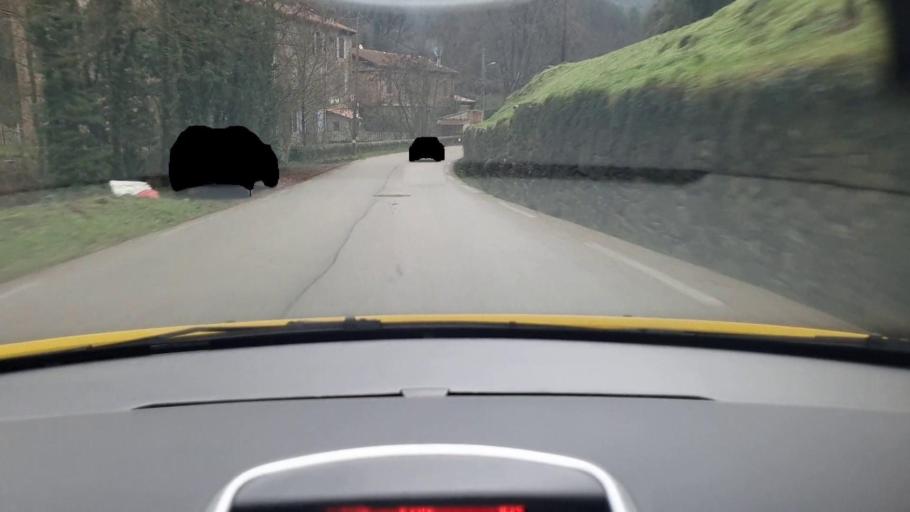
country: FR
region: Languedoc-Roussillon
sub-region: Departement du Gard
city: Besseges
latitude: 44.2794
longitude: 4.0895
